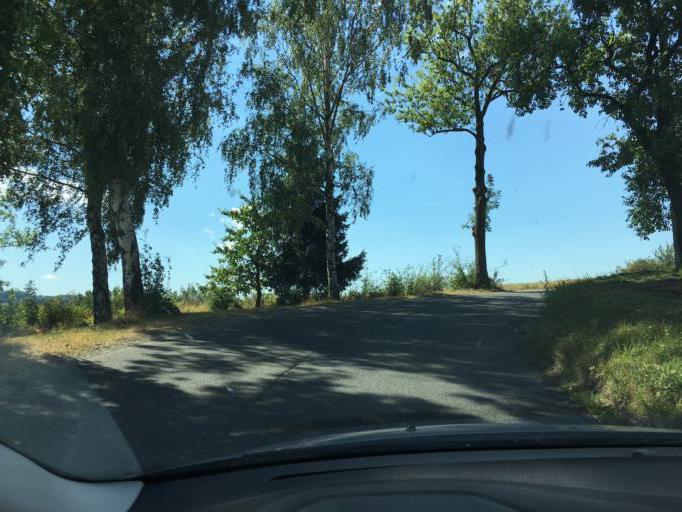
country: CZ
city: Plavy
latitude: 50.7022
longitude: 15.3480
